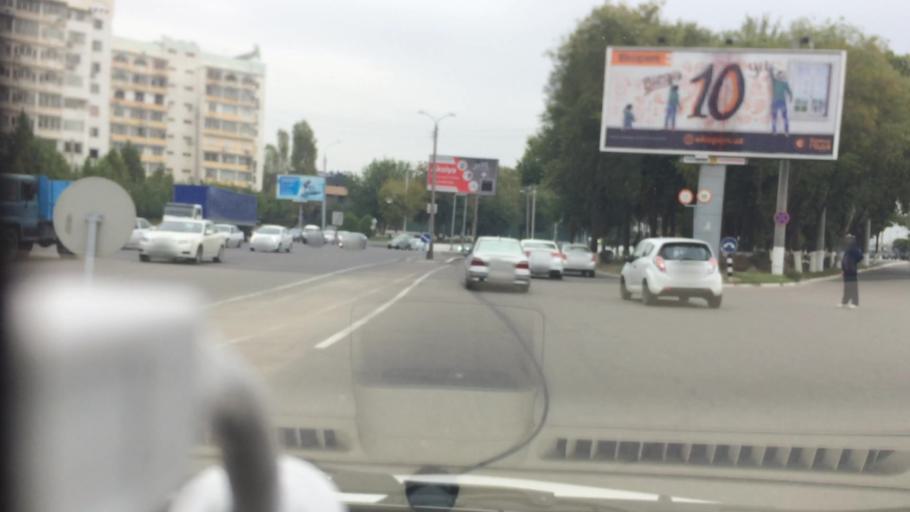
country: UZ
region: Toshkent Shahri
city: Tashkent
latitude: 41.2893
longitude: 69.2824
